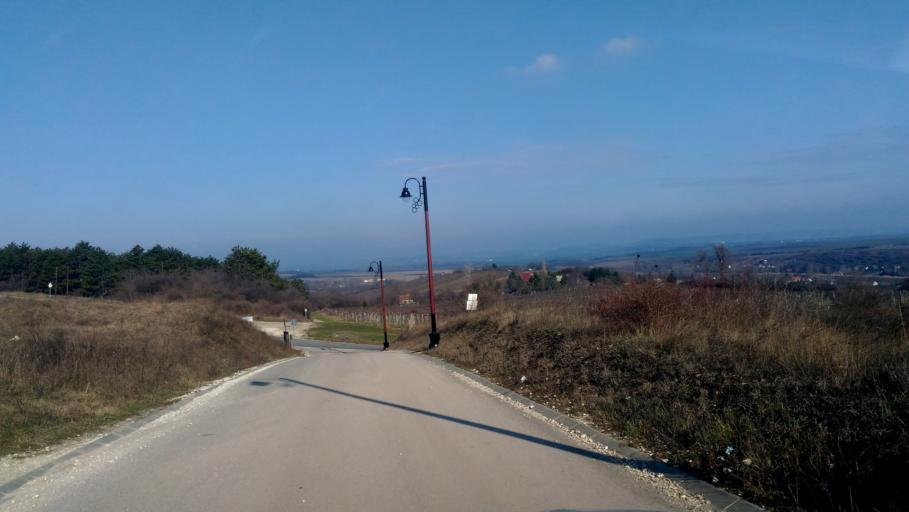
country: HU
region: Fejer
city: Etyek
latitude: 47.4428
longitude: 18.7370
